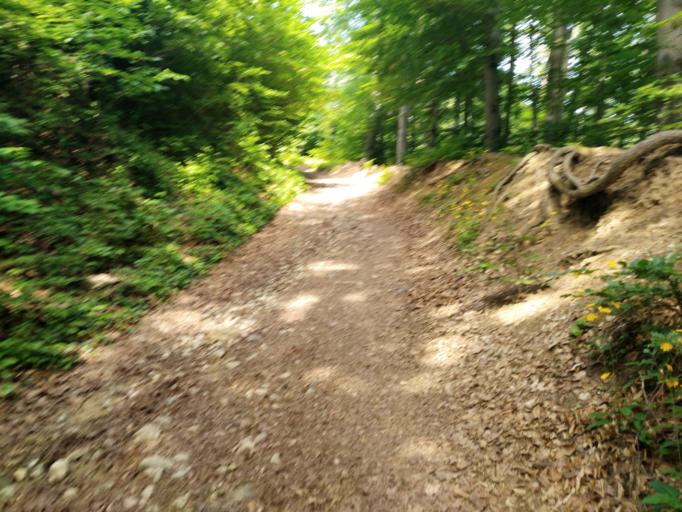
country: AT
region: Styria
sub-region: Graz Stadt
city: Wetzelsdorf
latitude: 47.0361
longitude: 15.3819
